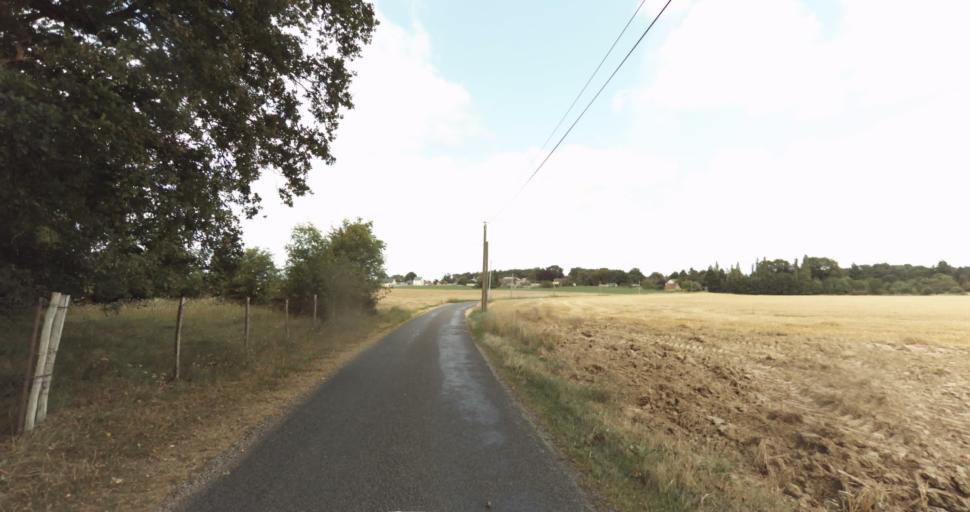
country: FR
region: Haute-Normandie
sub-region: Departement de l'Eure
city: Evreux
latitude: 48.9288
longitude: 1.2500
